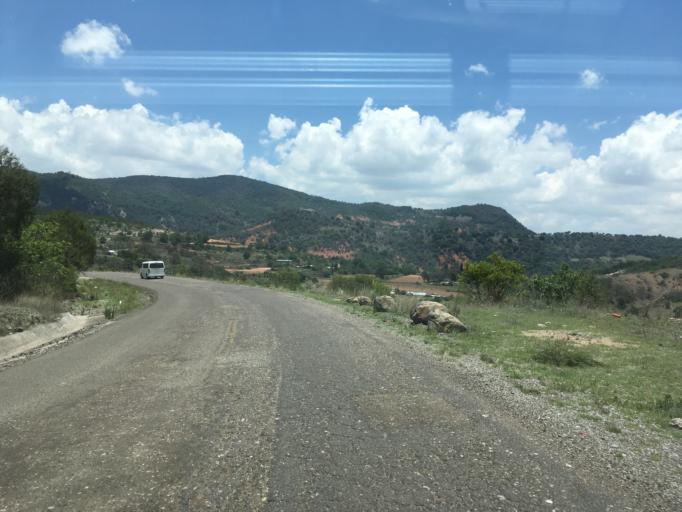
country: MX
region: Oaxaca
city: San Vicente Nunu
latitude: 17.5658
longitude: -97.3986
